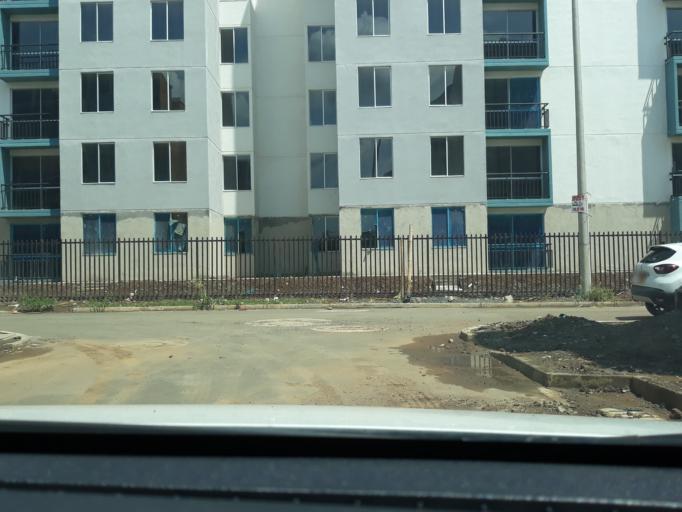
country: CO
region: Valle del Cauca
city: Cali
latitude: 3.3830
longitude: -76.5087
